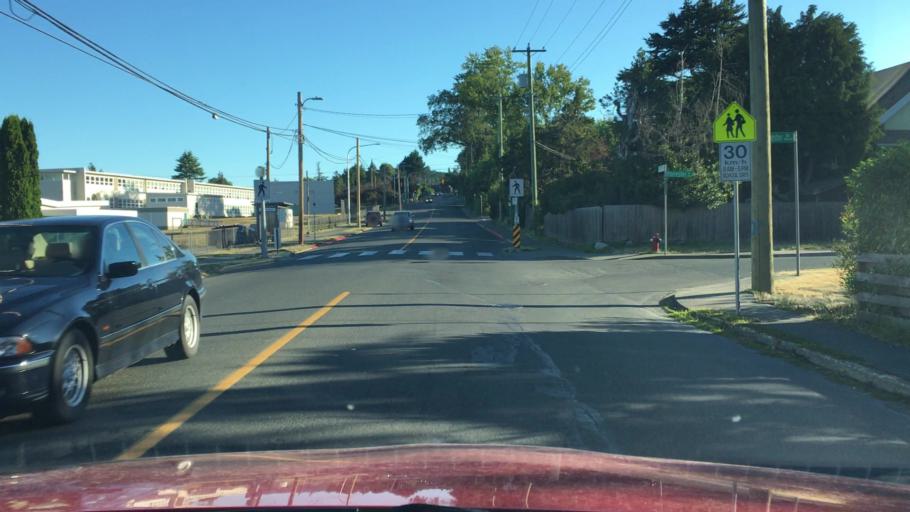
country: CA
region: British Columbia
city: Oak Bay
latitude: 48.4436
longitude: -123.3271
